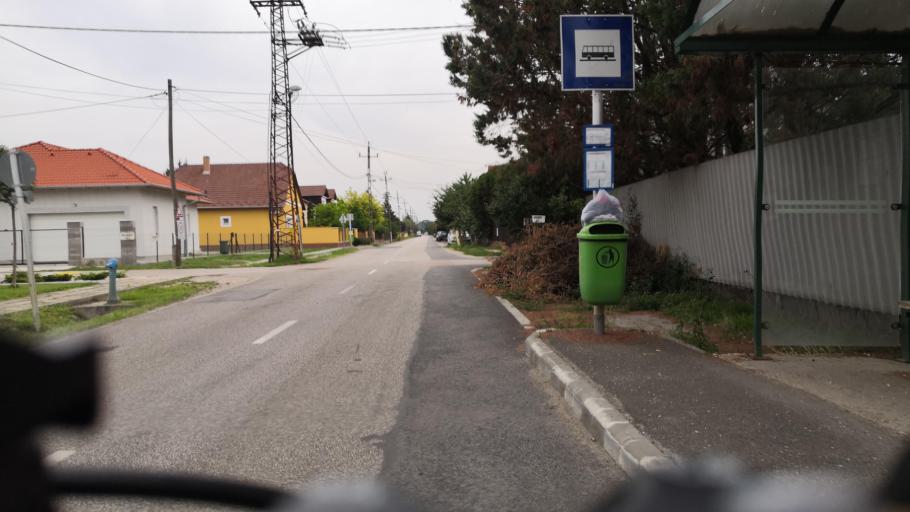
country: HU
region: Csongrad
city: Szeged
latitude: 46.2888
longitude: 20.1638
